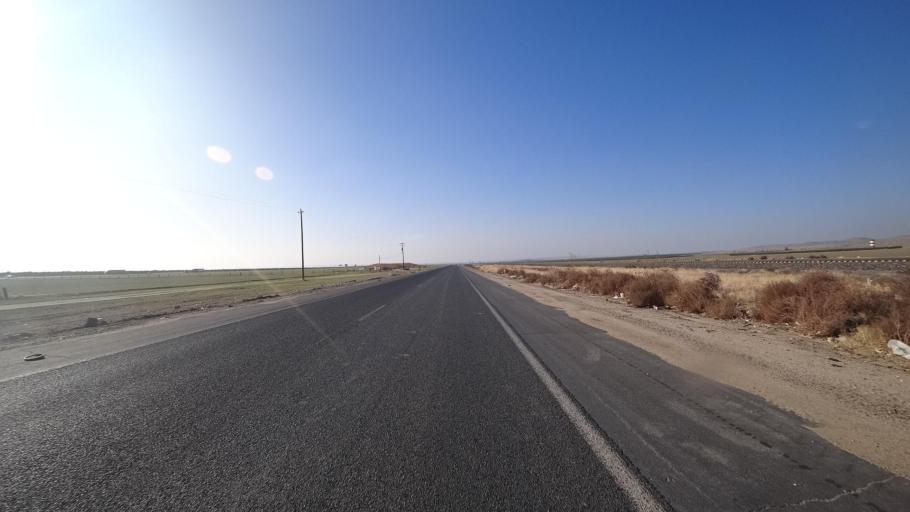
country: US
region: California
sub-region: Kern County
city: Arvin
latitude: 35.3328
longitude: -118.8089
